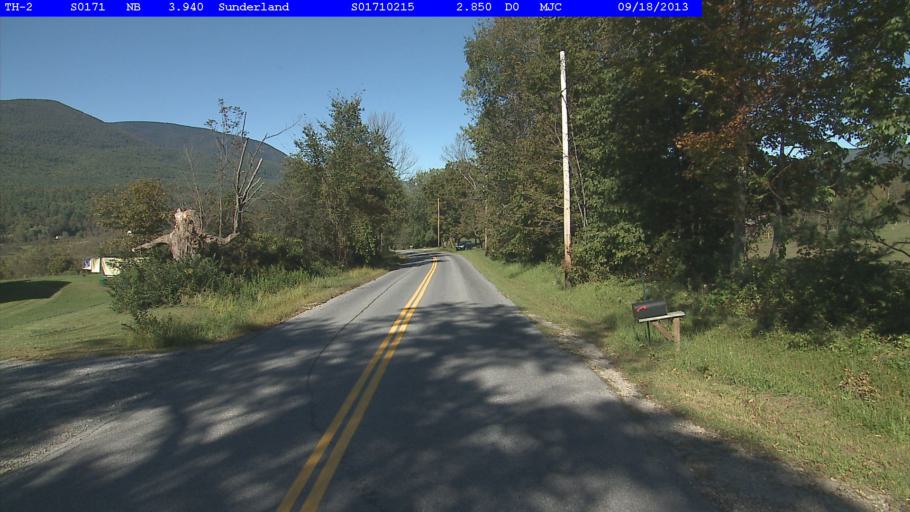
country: US
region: Vermont
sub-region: Bennington County
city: Arlington
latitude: 43.1049
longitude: -73.1209
